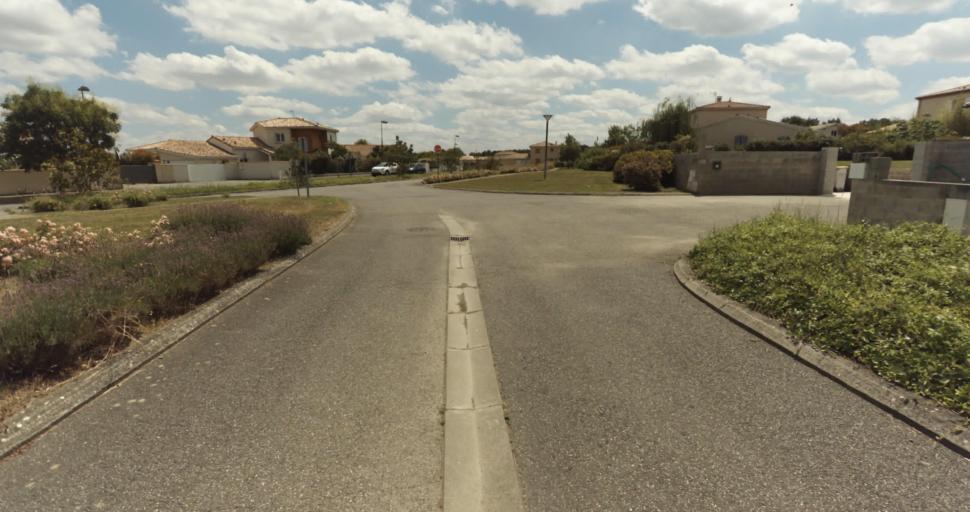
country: FR
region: Midi-Pyrenees
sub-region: Departement de la Haute-Garonne
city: Fontenilles
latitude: 43.5572
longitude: 1.1670
